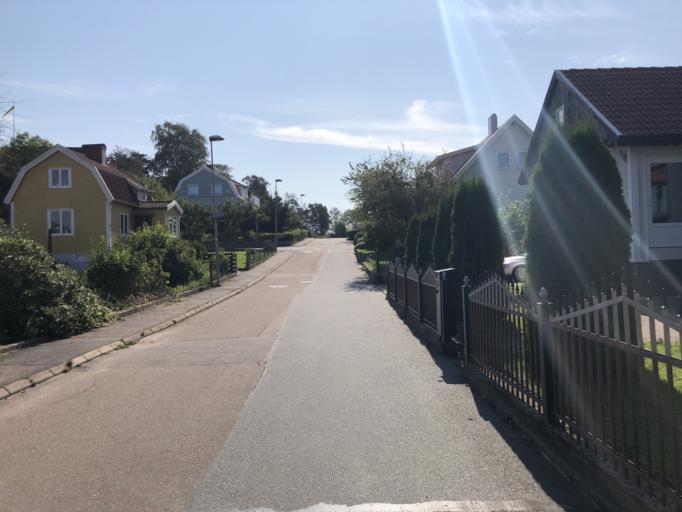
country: SE
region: Vaestra Goetaland
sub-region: Goteborg
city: Goeteborg
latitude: 57.7391
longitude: 11.9683
